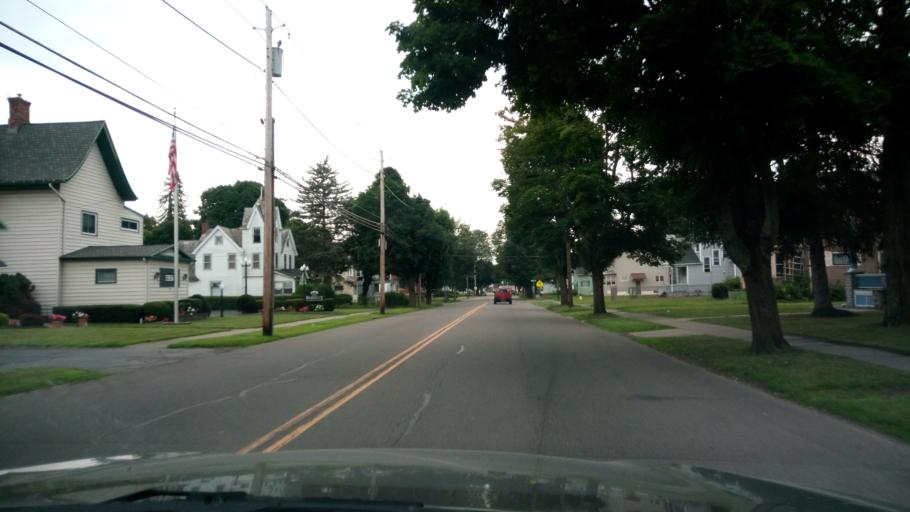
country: US
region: New York
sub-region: Chemung County
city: Elmira
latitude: 42.1050
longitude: -76.8051
